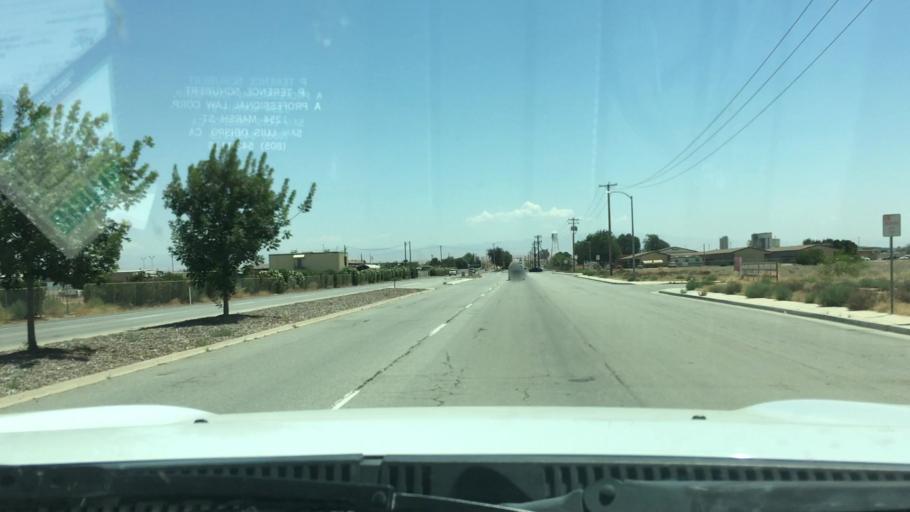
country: US
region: California
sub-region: Kern County
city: Shafter
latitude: 35.4994
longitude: -119.1775
